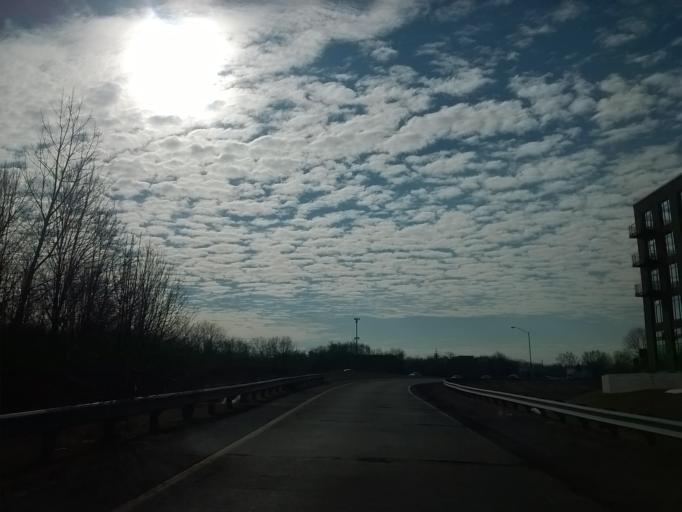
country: US
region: Indiana
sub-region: Marion County
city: Meridian Hills
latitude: 39.9116
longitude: -86.1157
